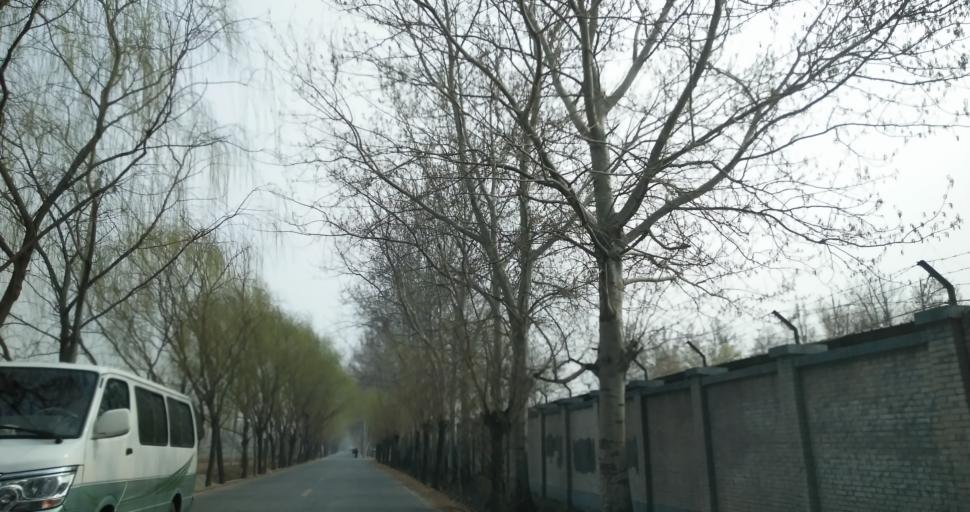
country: CN
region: Beijing
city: Qingyundian
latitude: 39.6988
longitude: 116.5020
